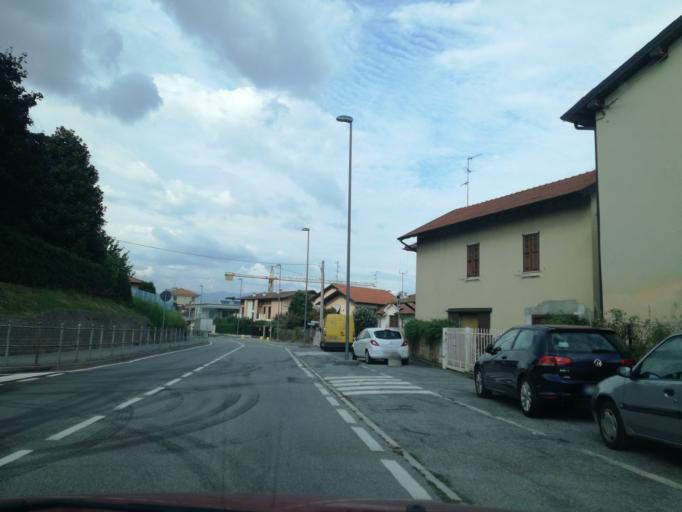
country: IT
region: Lombardy
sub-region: Provincia di Monza e Brianza
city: Vimercate
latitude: 45.6223
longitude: 9.3843
